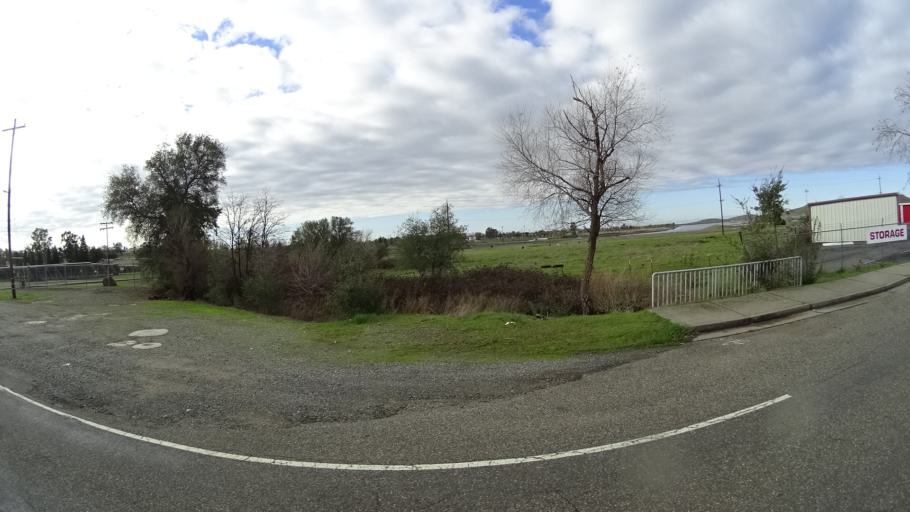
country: US
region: California
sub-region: Butte County
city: Thermalito
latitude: 39.5343
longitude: -121.5752
